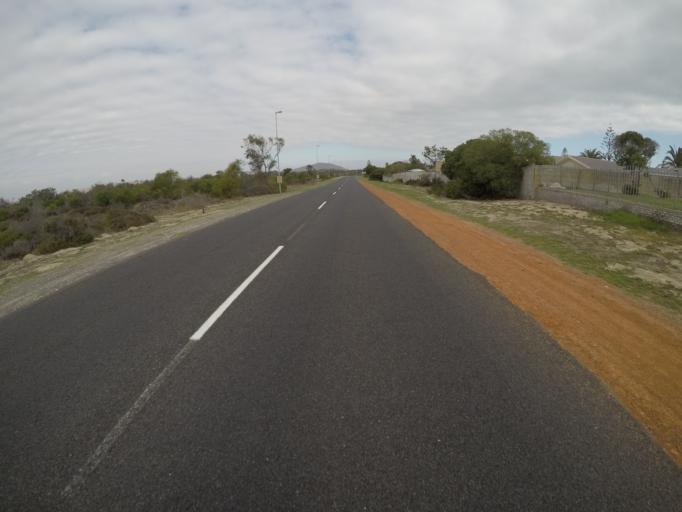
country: ZA
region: Western Cape
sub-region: City of Cape Town
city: Atlantis
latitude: -33.7057
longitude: 18.4466
